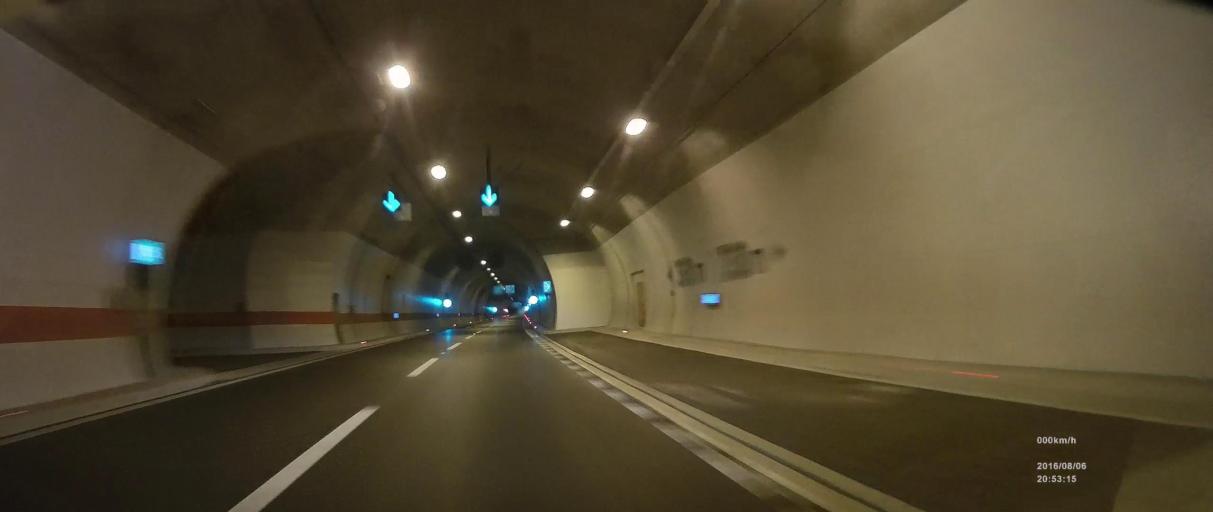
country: BA
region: Federation of Bosnia and Herzegovina
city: Ljubuski
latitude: 43.1408
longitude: 17.4855
